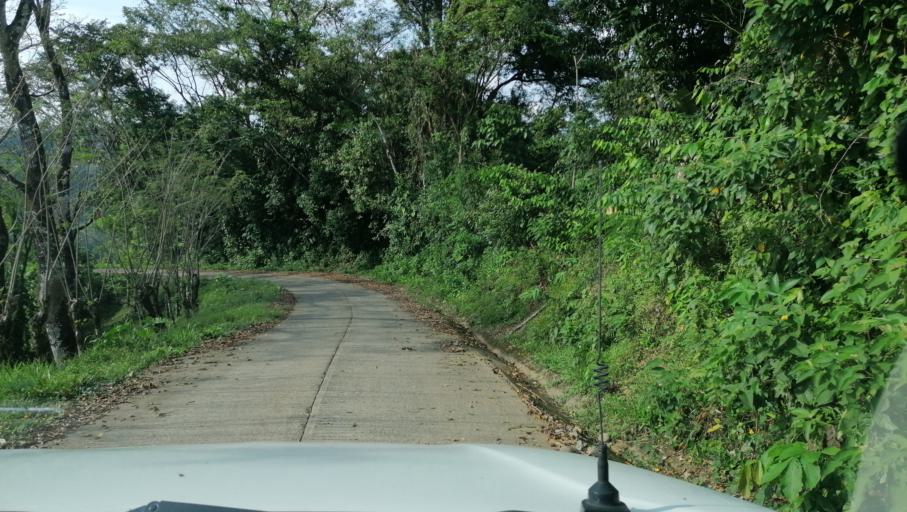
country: MX
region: Chiapas
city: Ostuacan
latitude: 17.4684
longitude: -93.2342
